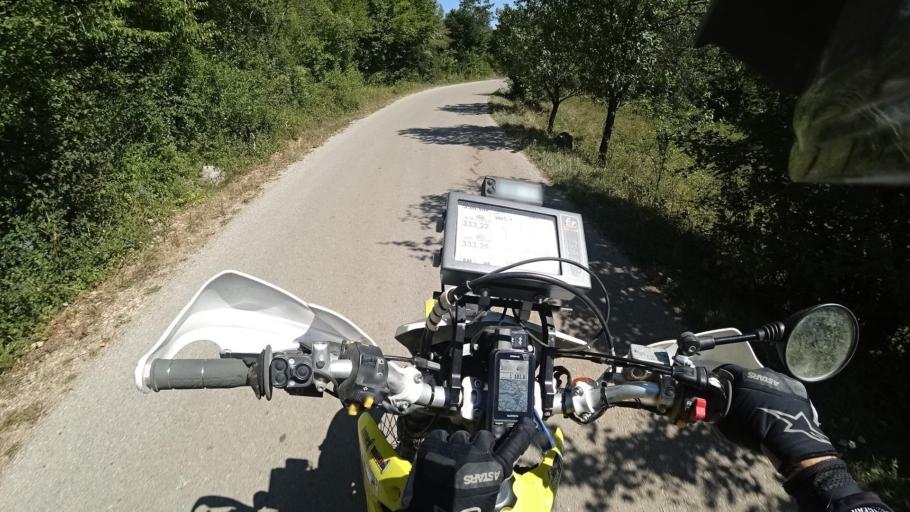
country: HR
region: Licko-Senjska
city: Popovaca
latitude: 44.7061
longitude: 15.2424
